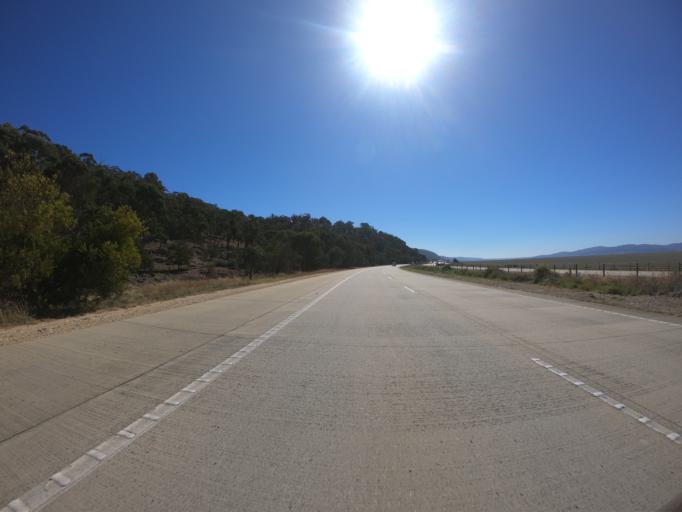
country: AU
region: New South Wales
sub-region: Yass Valley
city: Gundaroo
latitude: -35.0894
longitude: 149.3747
